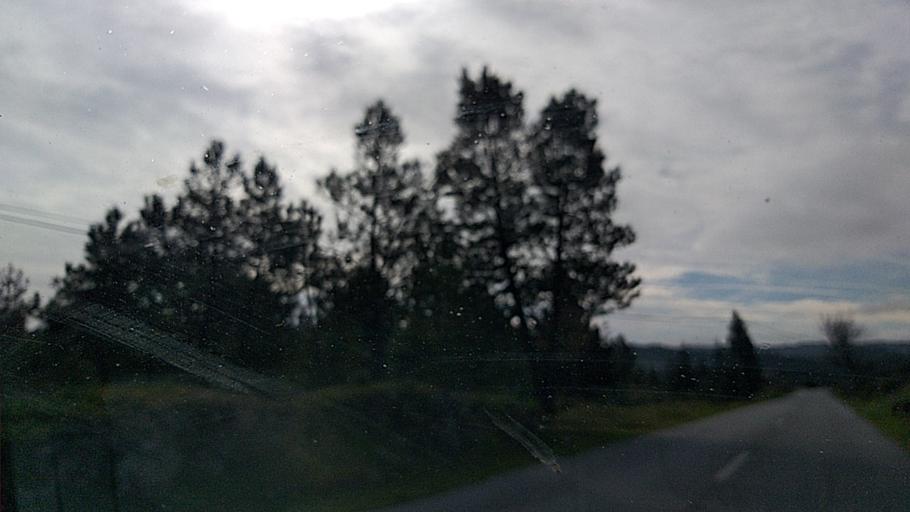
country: PT
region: Guarda
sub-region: Fornos de Algodres
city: Fornos de Algodres
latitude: 40.6733
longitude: -7.5290
